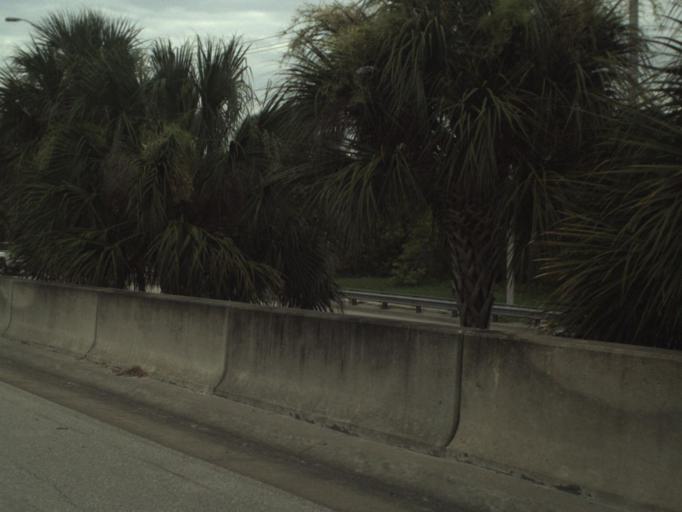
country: US
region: Florida
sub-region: Palm Beach County
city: Royal Palm Beach
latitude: 26.6803
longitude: -80.1990
